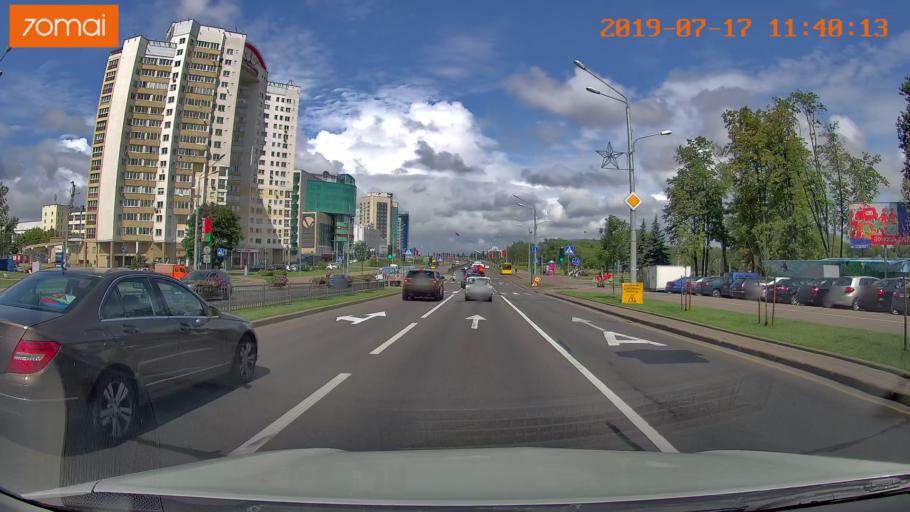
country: BY
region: Minsk
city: Minsk
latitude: 53.9198
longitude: 27.5309
